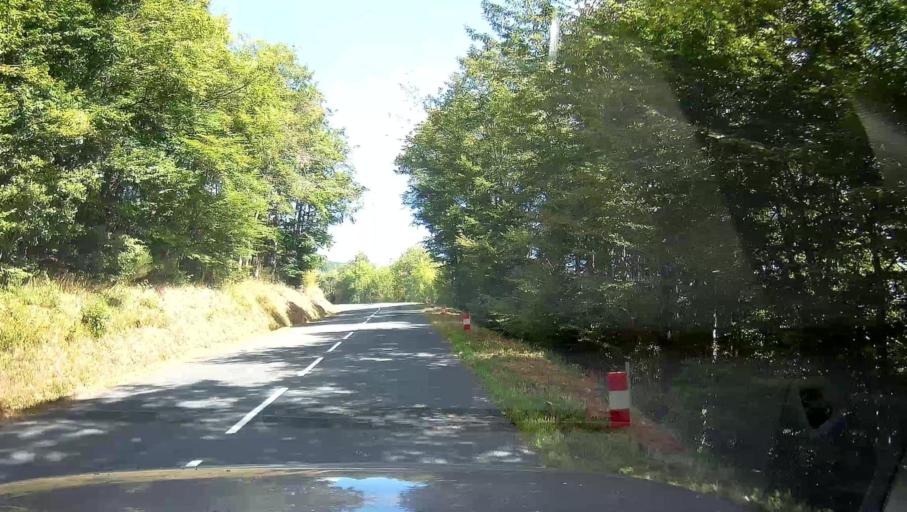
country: FR
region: Rhone-Alpes
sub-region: Departement du Rhone
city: Cogny
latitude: 45.9871
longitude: 4.5731
